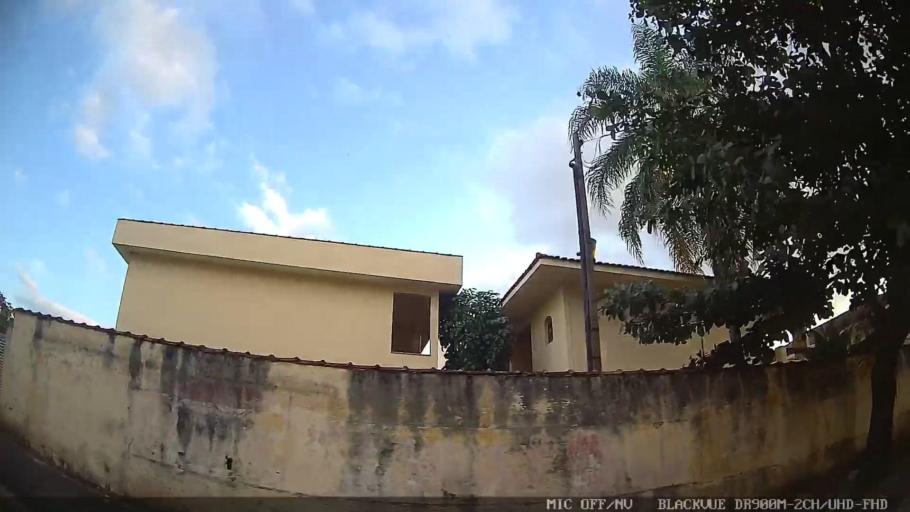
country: BR
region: Sao Paulo
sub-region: Guaruja
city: Guaruja
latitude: -23.9850
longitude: -46.2068
